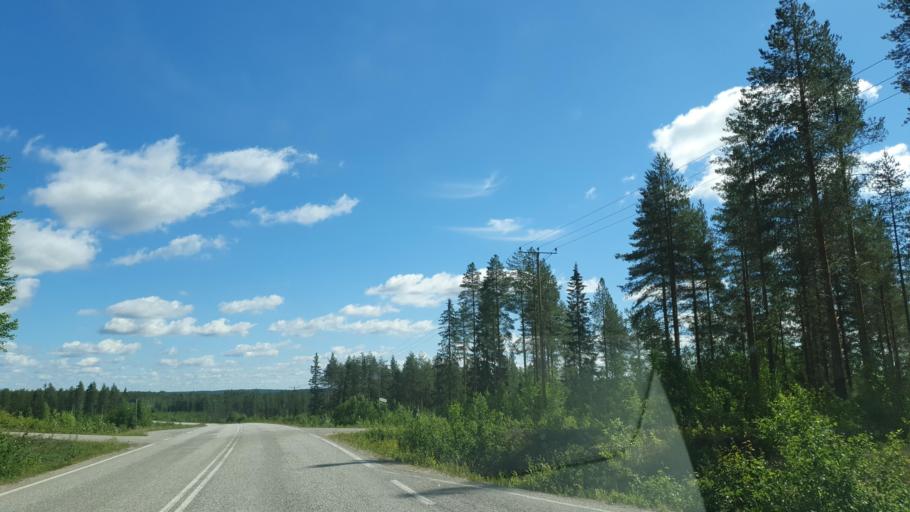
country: FI
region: Kainuu
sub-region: Kehys-Kainuu
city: Kuhmo
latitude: 64.2087
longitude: 29.7531
